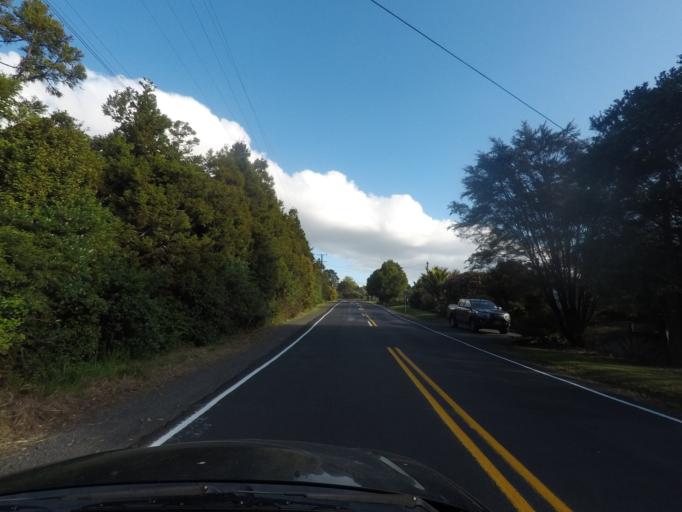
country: NZ
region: Auckland
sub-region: Auckland
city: Waitakere
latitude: -36.9163
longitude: 174.6150
